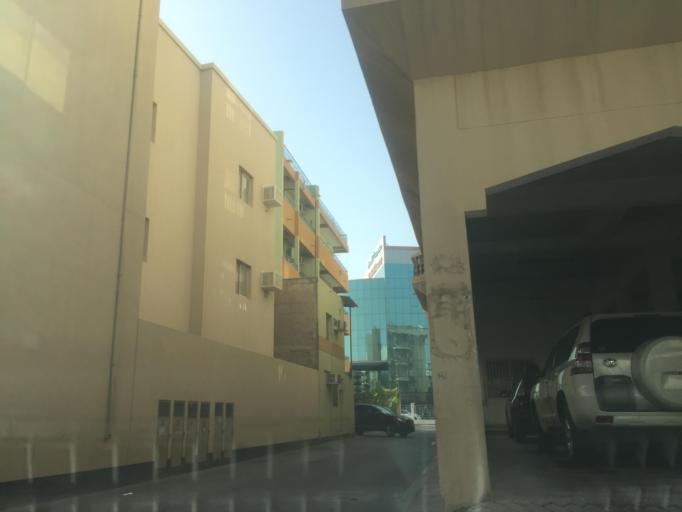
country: BH
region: Manama
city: Manama
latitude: 26.2197
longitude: 50.5759
